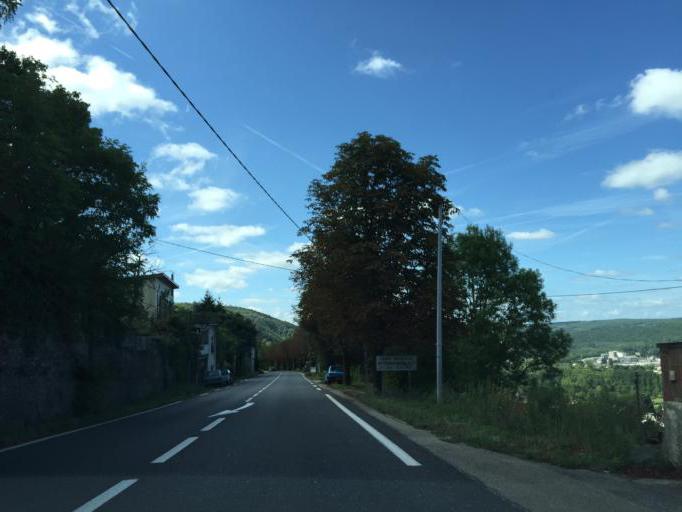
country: FR
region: Midi-Pyrenees
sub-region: Departement de l'Aveyron
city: Villefranche-de-Rouergue
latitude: 44.3439
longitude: 2.0394
